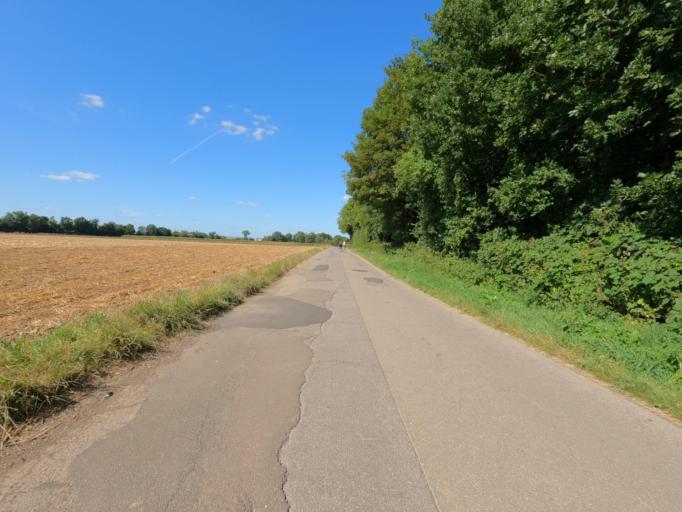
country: DE
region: North Rhine-Westphalia
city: Julich
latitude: 50.9262
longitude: 6.3422
